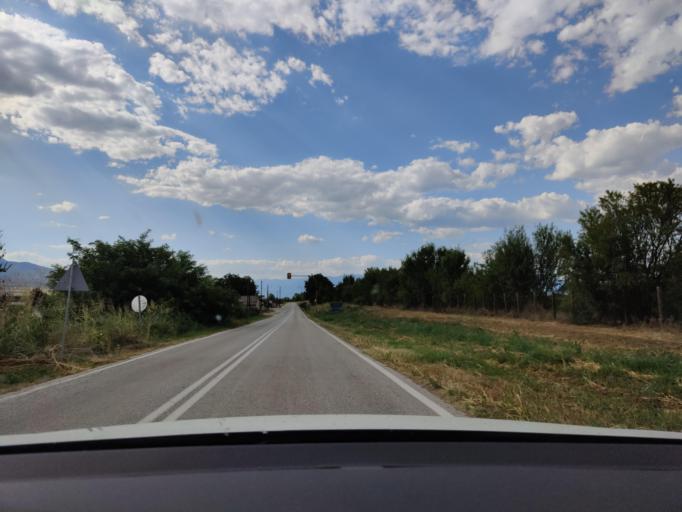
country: GR
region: Central Macedonia
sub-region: Nomos Serron
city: Strymoniko
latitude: 41.0841
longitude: 23.2881
